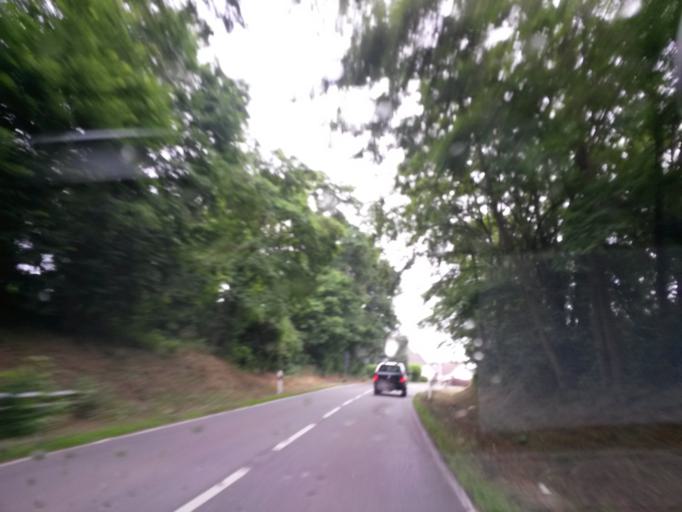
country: DE
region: North Rhine-Westphalia
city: Lohmar
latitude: 50.8455
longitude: 7.2355
